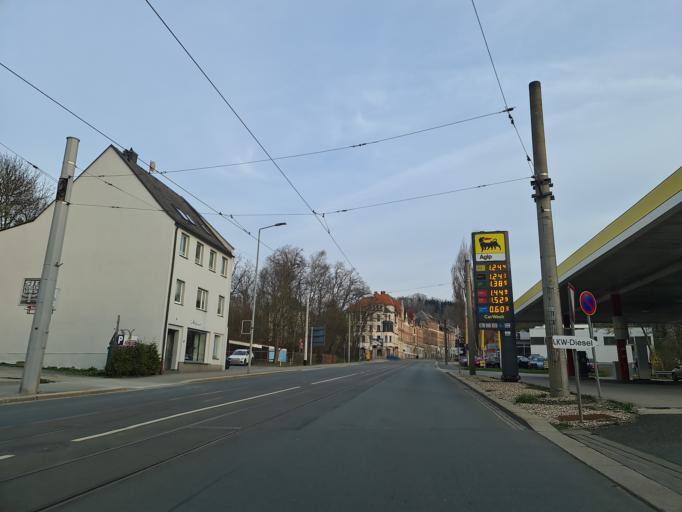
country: DE
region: Saxony
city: Plauen
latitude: 50.4854
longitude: 12.1391
